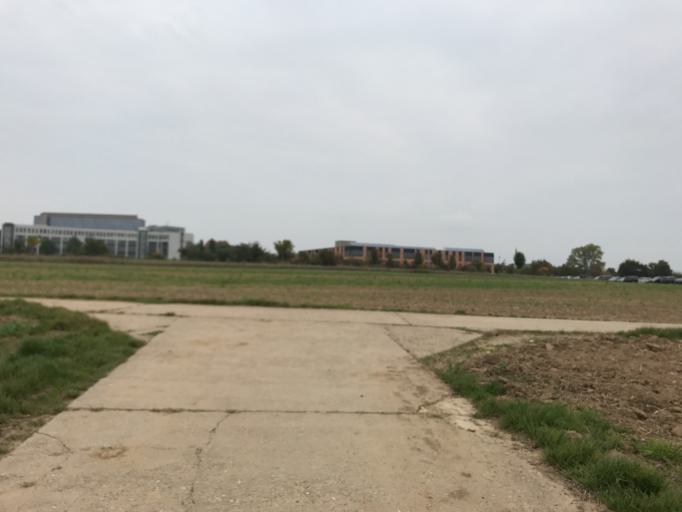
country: DE
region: Rheinland-Pfalz
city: Klein-Winternheim
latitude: 49.9573
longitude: 8.2118
